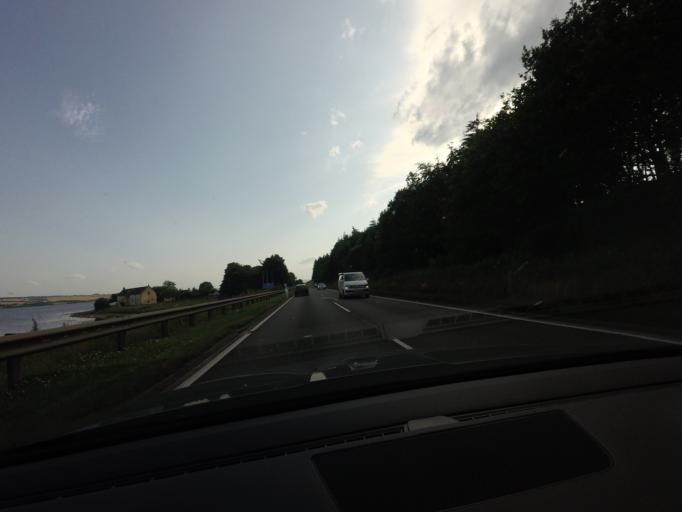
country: GB
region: Scotland
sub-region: Highland
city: Evanton
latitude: 57.6420
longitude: -4.3472
